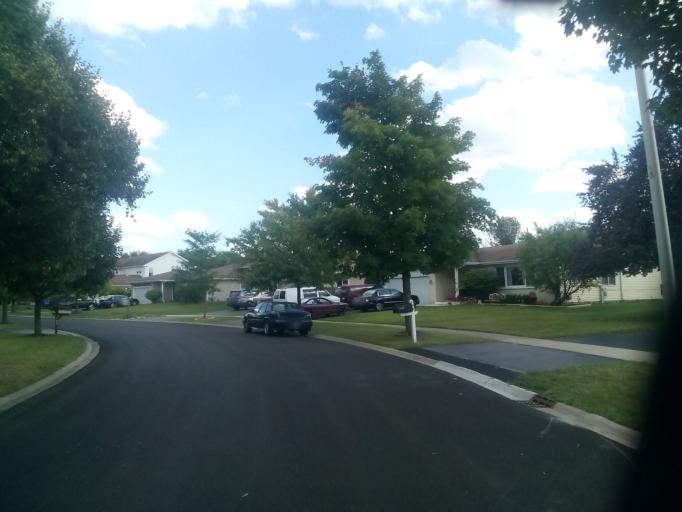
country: US
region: Illinois
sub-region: Will County
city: Romeoville
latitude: 41.6983
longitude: -88.1462
